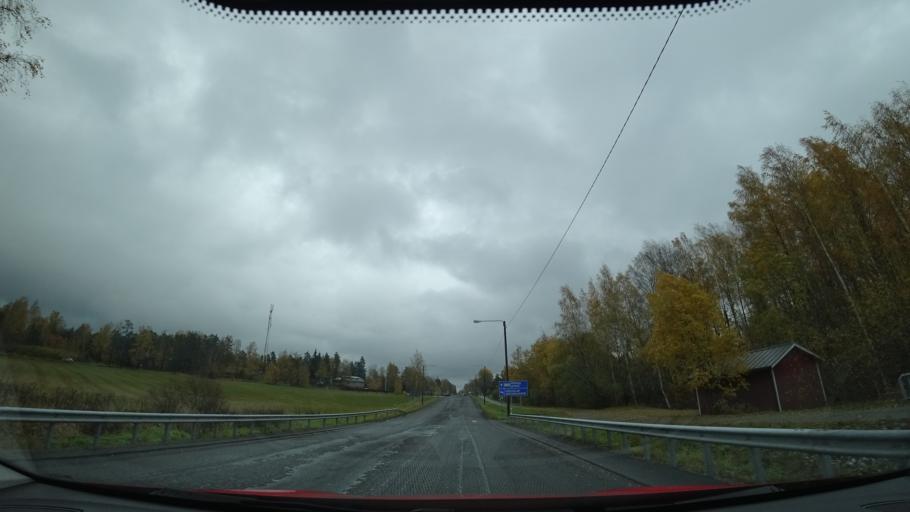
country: FI
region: Uusimaa
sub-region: Helsinki
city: Vantaa
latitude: 60.2503
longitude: 25.1688
